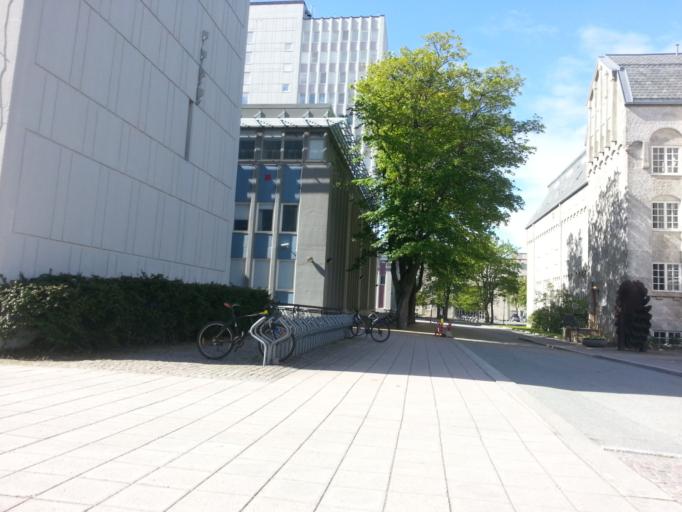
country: NO
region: Sor-Trondelag
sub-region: Trondheim
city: Trondheim
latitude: 63.4170
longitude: 10.4050
